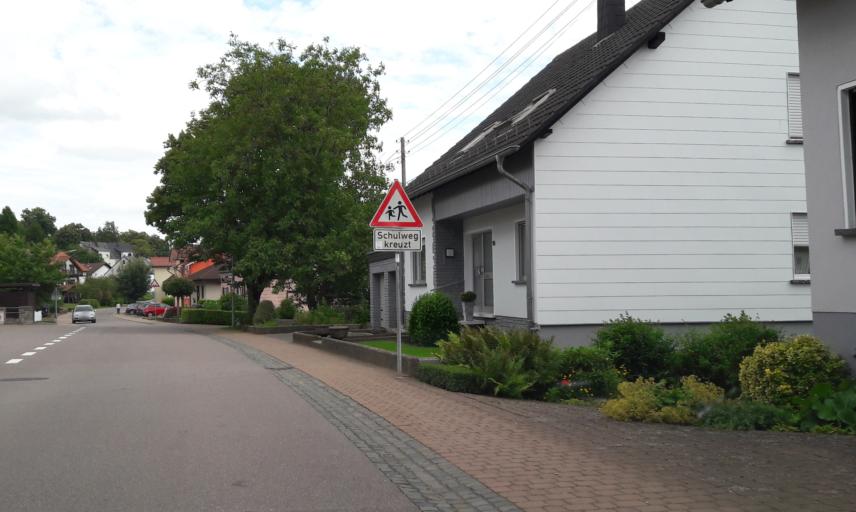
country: DE
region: Saarland
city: Tholey
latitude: 49.4820
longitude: 7.0353
